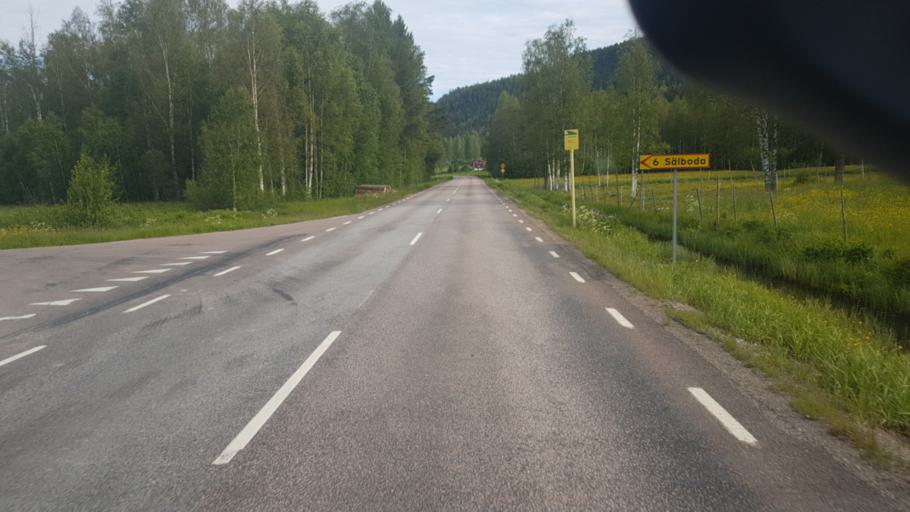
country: SE
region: Vaermland
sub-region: Arvika Kommun
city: Arvika
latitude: 59.7455
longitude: 12.6391
